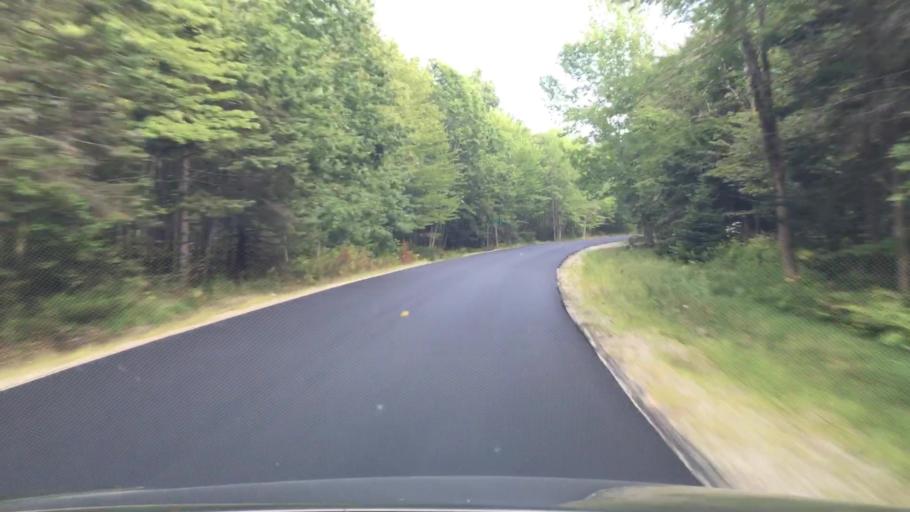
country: US
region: Maine
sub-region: Hancock County
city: Orland
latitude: 44.5438
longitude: -68.6177
